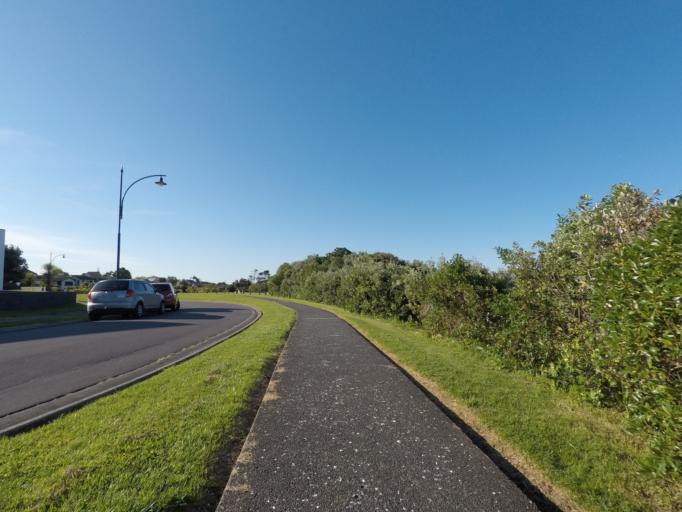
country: NZ
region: Auckland
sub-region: Auckland
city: Rosebank
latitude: -36.8345
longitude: 174.6619
